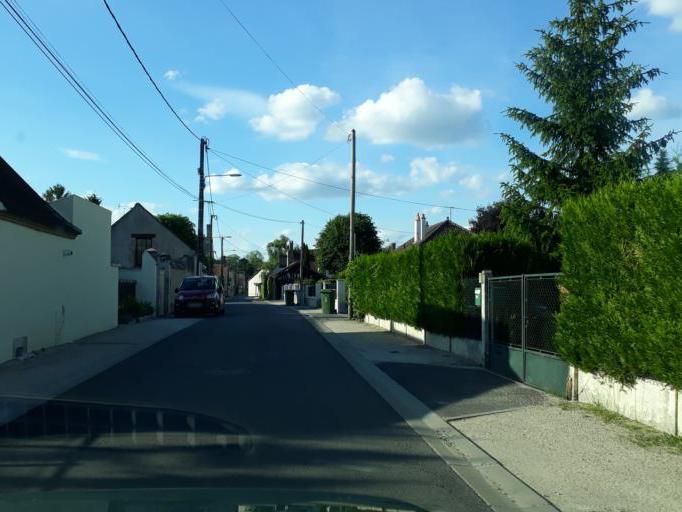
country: FR
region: Centre
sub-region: Departement du Loiret
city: Saint-Pryve-Saint-Mesmin
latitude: 47.8642
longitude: 1.8697
